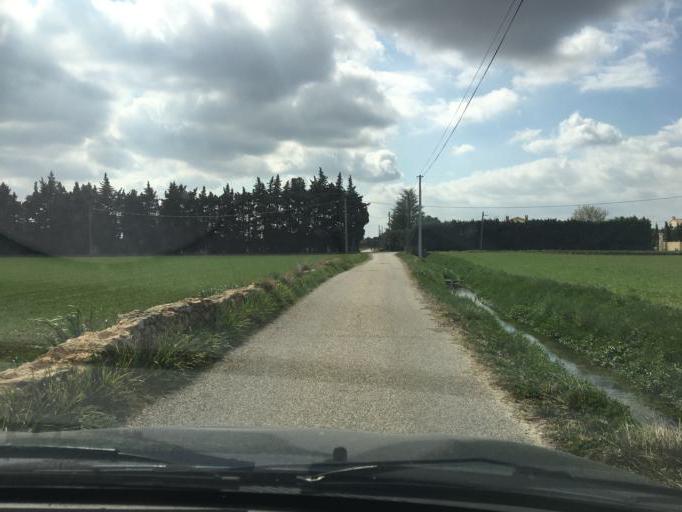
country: FR
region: Provence-Alpes-Cote d'Azur
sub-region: Departement du Vaucluse
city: Serignan-du-Comtat
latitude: 44.1831
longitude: 4.8360
